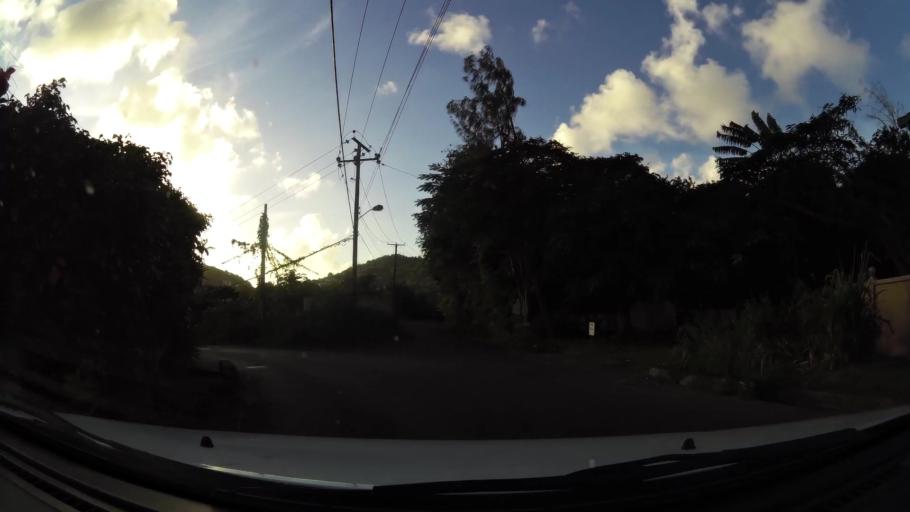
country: LC
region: Gros-Islet
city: Gros Islet
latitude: 14.0615
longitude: -60.9432
